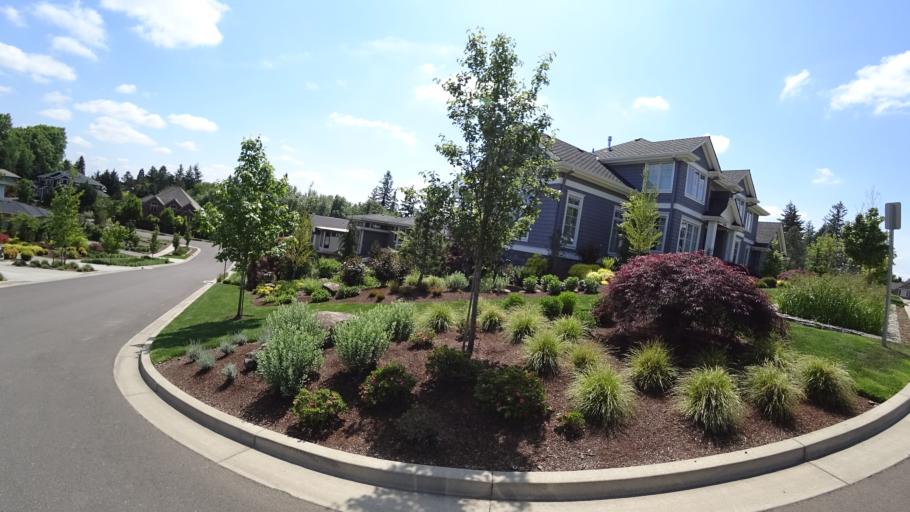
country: US
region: Oregon
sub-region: Clackamas County
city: Lake Oswego
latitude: 45.4323
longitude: -122.6958
